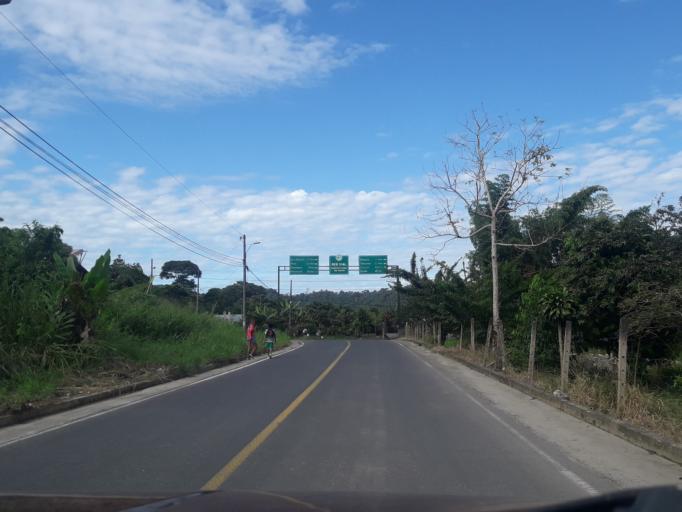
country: EC
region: Napo
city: Tena
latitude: -0.9812
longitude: -77.8439
